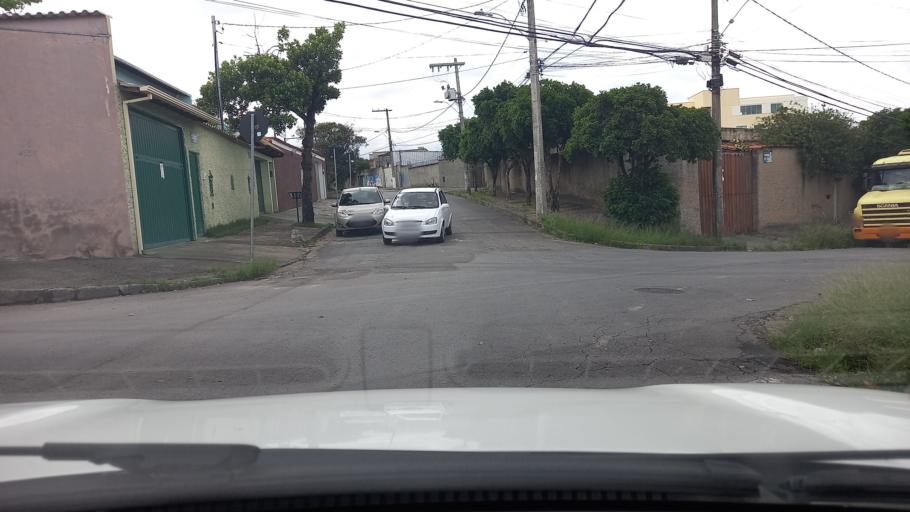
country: BR
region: Minas Gerais
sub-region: Contagem
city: Contagem
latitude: -19.9042
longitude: -44.0041
